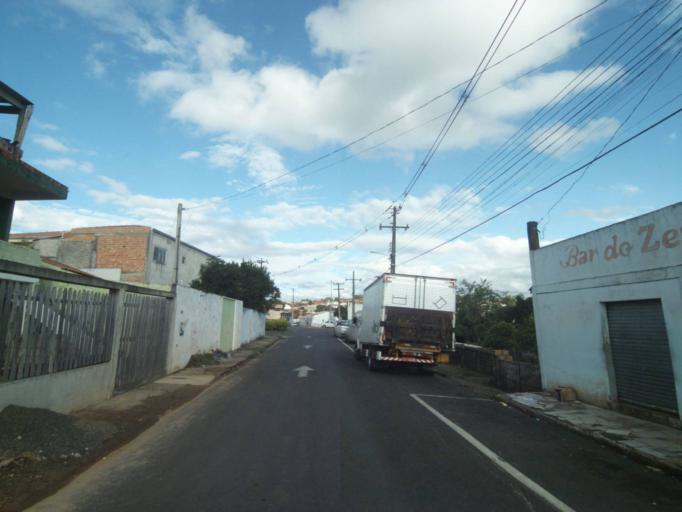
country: BR
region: Parana
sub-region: Telemaco Borba
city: Telemaco Borba
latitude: -24.3372
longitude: -50.6174
